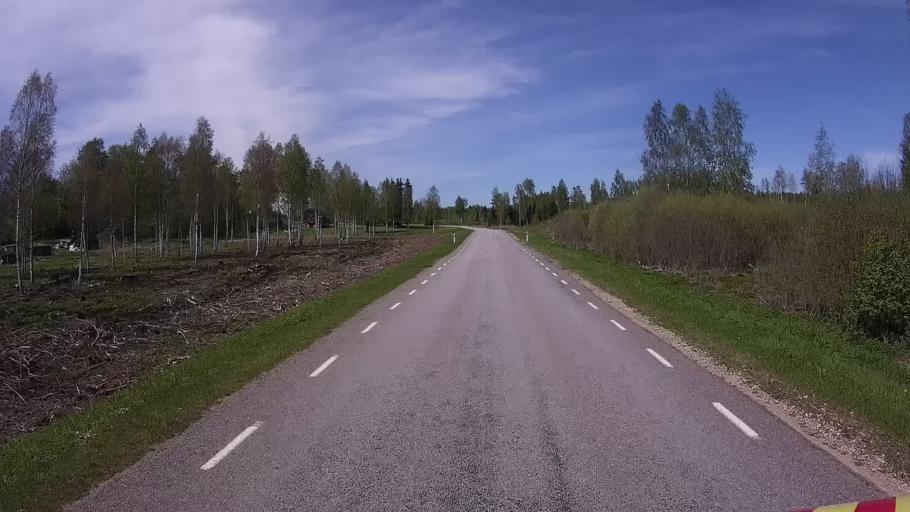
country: EE
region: Vorumaa
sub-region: Antsla vald
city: Vana-Antsla
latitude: 57.6415
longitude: 26.3303
